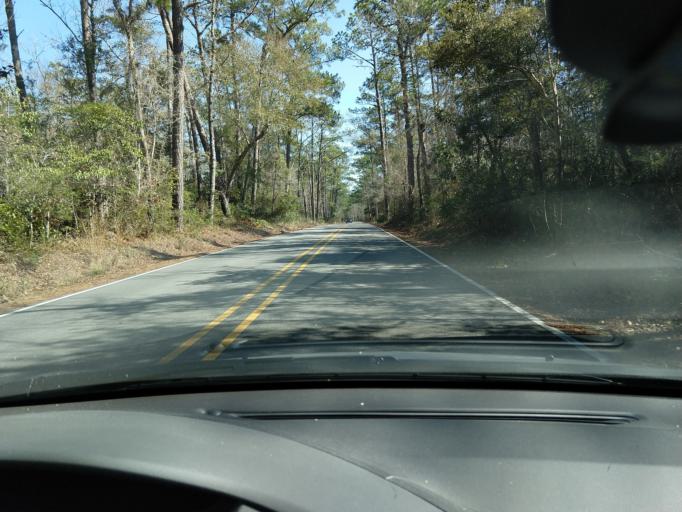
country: US
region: Mississippi
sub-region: Jackson County
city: Gulf Park Estates
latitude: 30.3959
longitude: -88.7823
